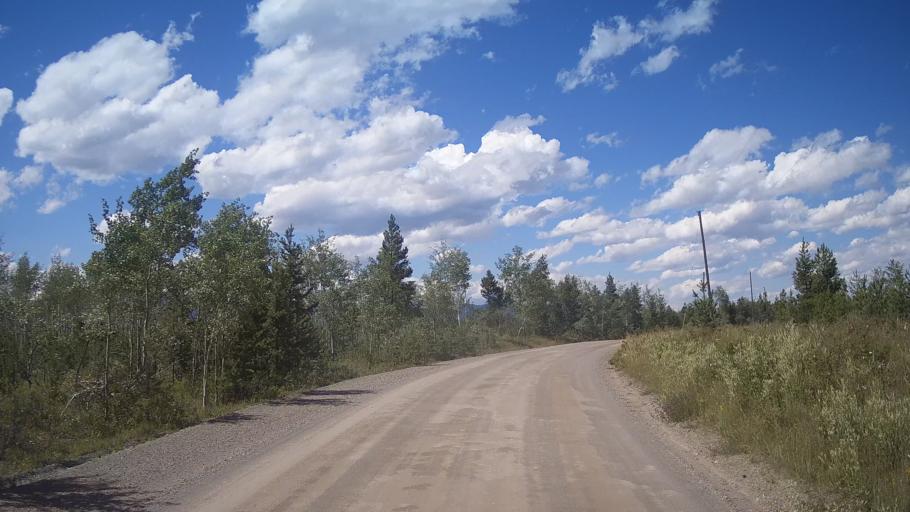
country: CA
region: British Columbia
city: Cache Creek
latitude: 51.2514
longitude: -121.6712
